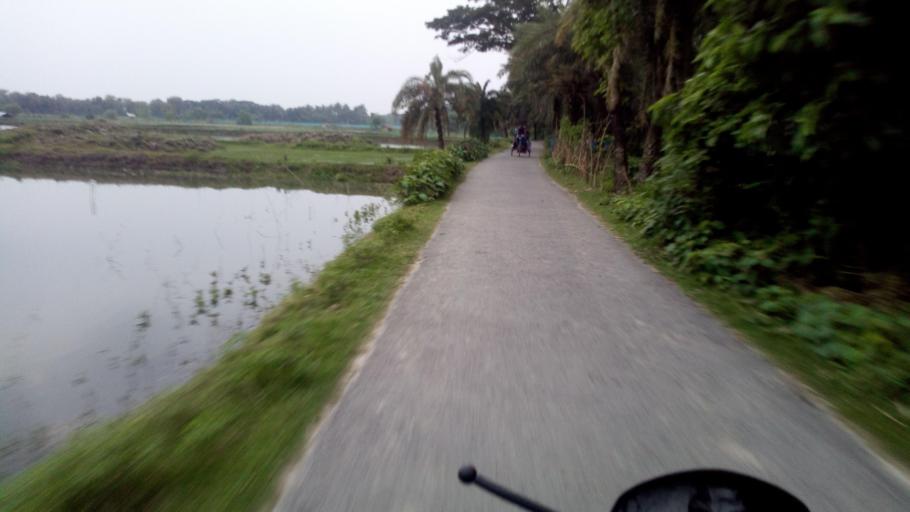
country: BD
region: Khulna
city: Phultala
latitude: 22.7664
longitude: 89.4073
